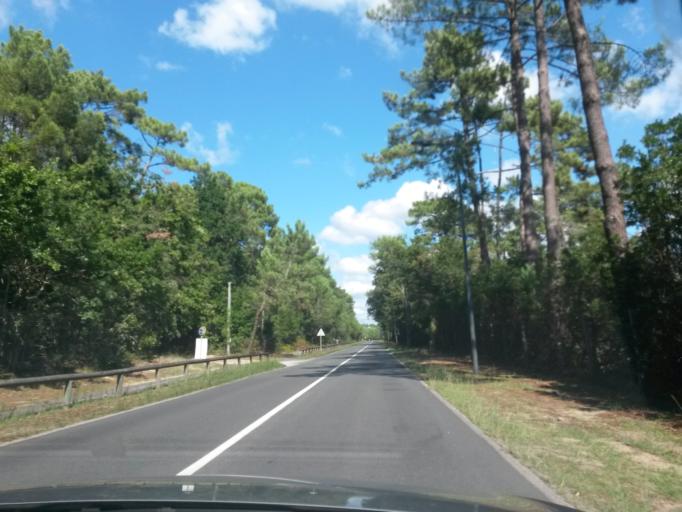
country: FR
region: Aquitaine
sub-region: Departement de la Gironde
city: Ares
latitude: 44.7372
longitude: -1.1949
